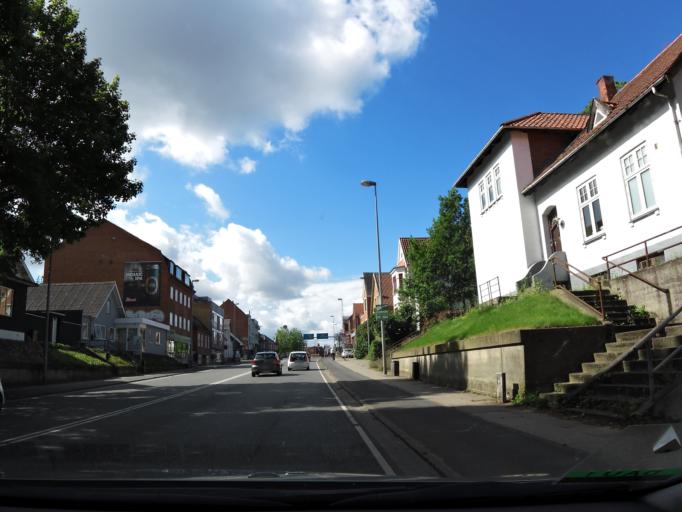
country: DK
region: South Denmark
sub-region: Odense Kommune
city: Odense
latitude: 55.3761
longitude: 10.3707
